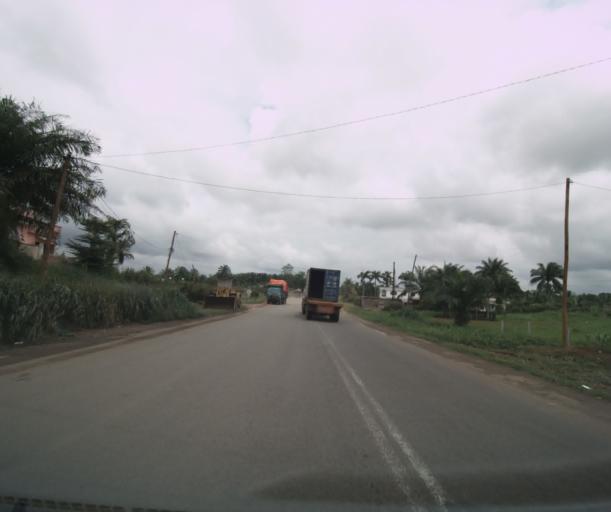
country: CM
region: Littoral
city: Edea
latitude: 3.7863
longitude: 10.1476
